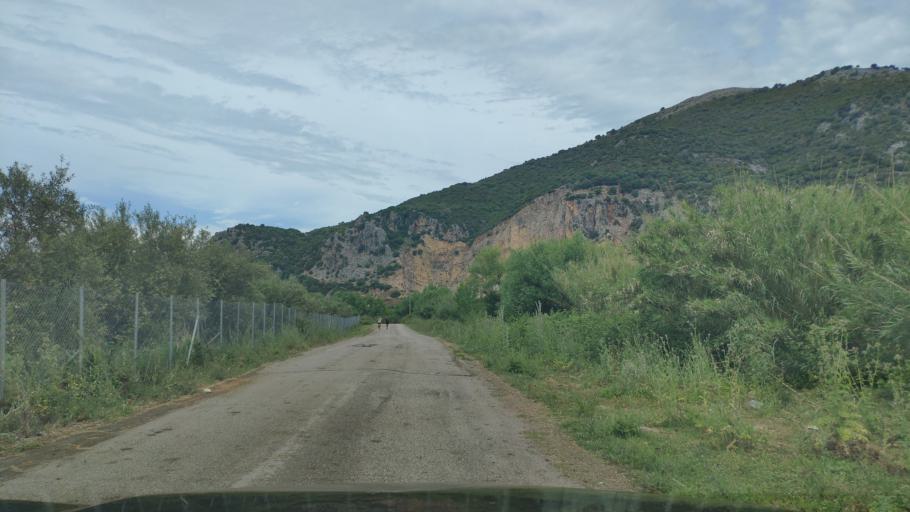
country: GR
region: West Greece
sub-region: Nomos Aitolias kai Akarnanias
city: Vonitsa
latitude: 38.9113
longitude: 20.9075
